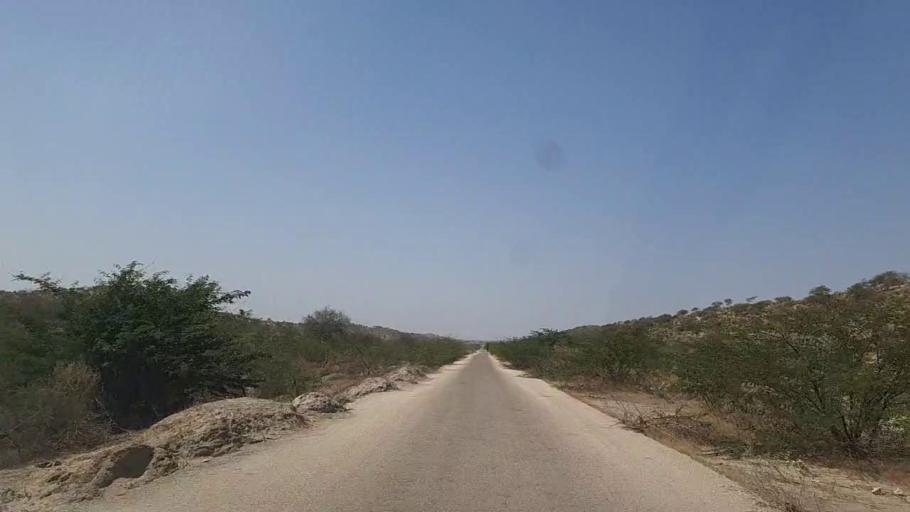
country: PK
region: Sindh
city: Diplo
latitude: 24.5188
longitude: 69.3492
